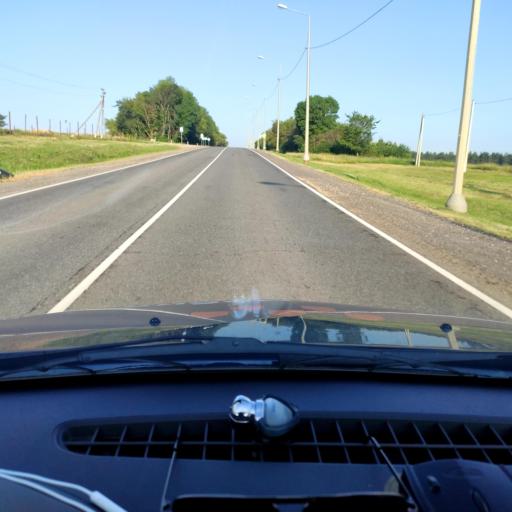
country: RU
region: Orjol
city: Livny
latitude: 52.4273
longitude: 37.7701
